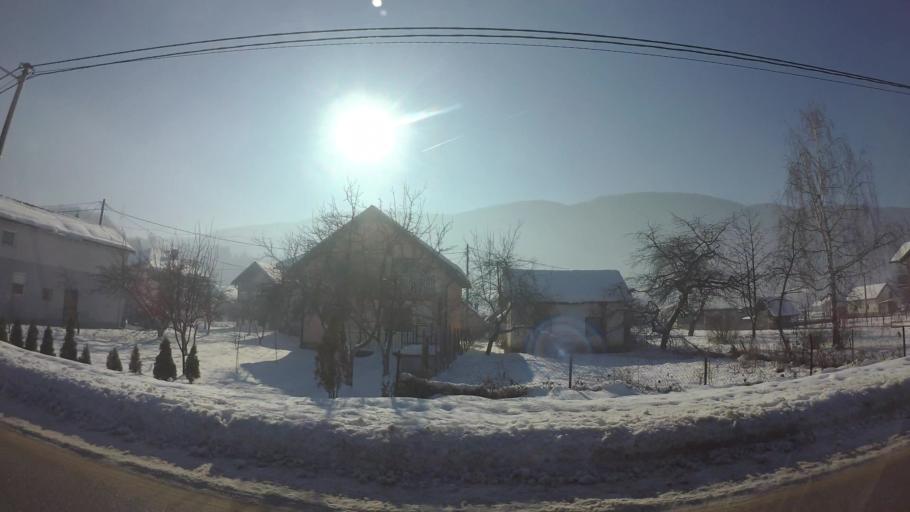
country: BA
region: Federation of Bosnia and Herzegovina
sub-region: Kanton Sarajevo
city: Sarajevo
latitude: 43.7908
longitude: 18.3442
